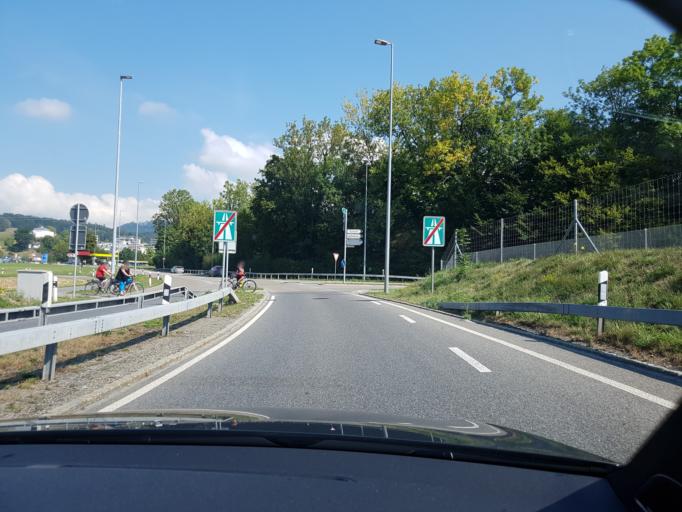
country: CH
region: Saint Gallen
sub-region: Wahlkreis See-Gaster
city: Schmerikon
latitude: 47.2385
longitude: 8.9504
